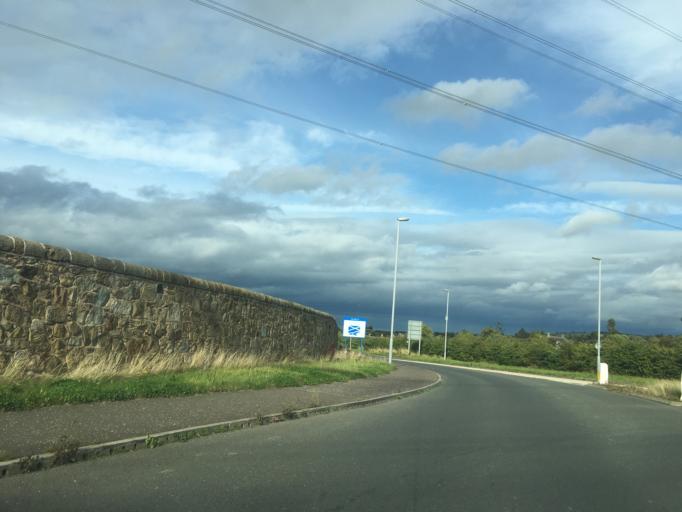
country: GB
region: Scotland
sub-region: Midlothian
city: Dalkeith
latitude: 55.9118
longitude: -3.0456
